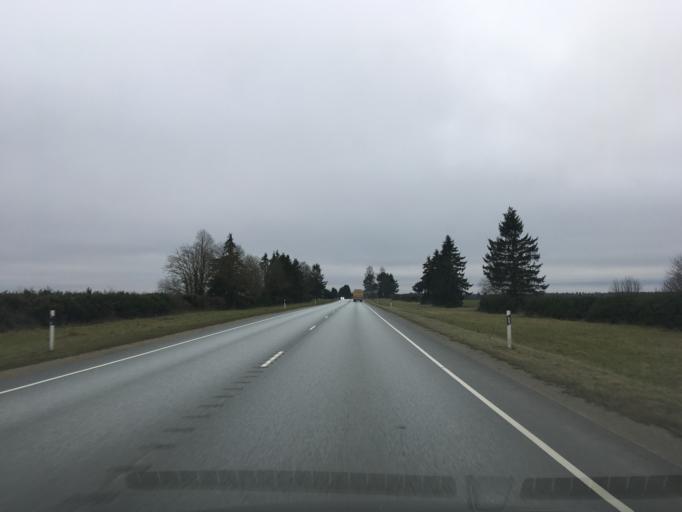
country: EE
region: Laeaene-Virumaa
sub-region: Viru-Nigula vald
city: Kunda
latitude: 59.3932
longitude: 26.6220
